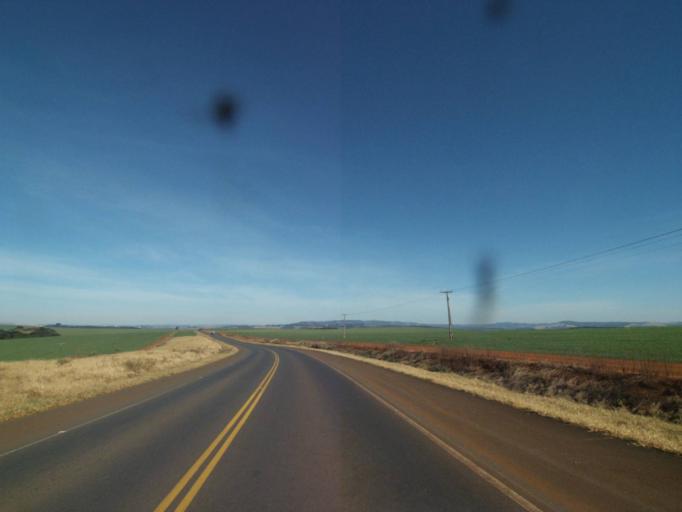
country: BR
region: Parana
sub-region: Tibagi
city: Tibagi
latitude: -24.4397
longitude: -50.4229
